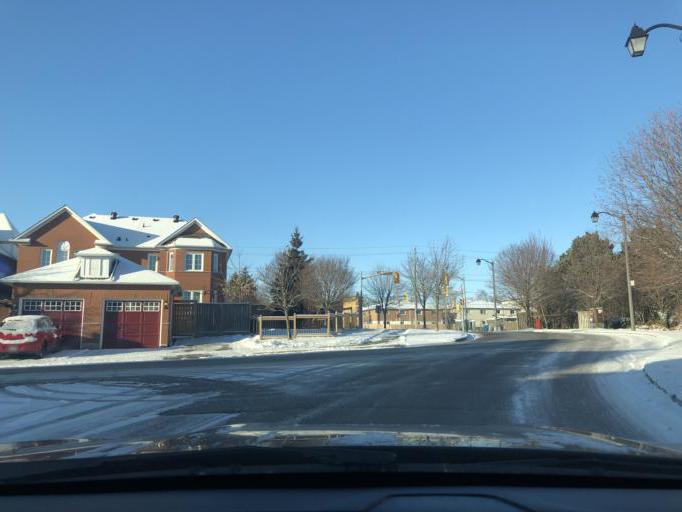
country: CA
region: Ontario
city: Pickering
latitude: 43.7814
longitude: -79.1363
